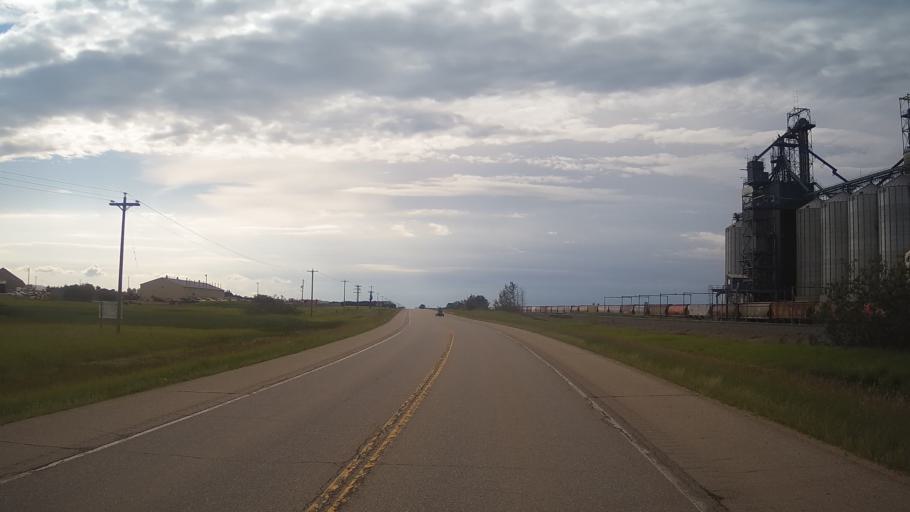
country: CA
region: Alberta
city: Viking
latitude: 53.0979
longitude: -111.7949
